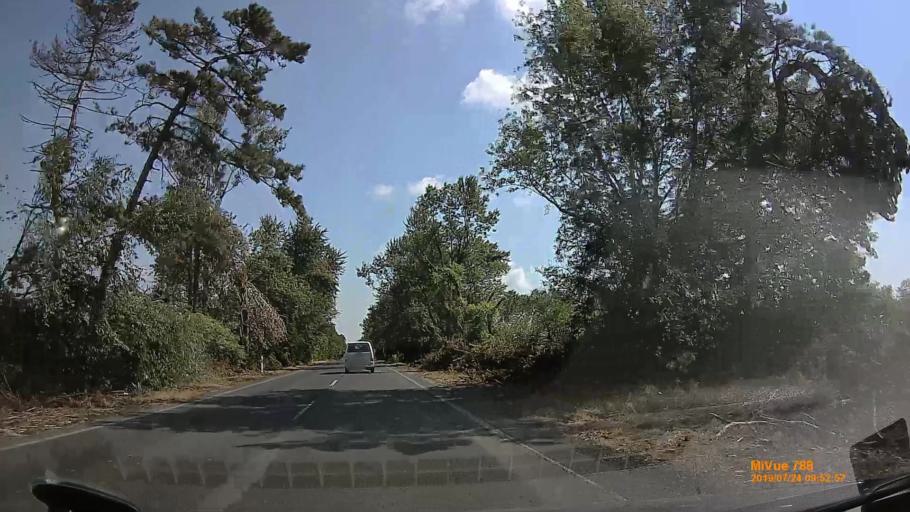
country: HU
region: Szabolcs-Szatmar-Bereg
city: Nyirmada
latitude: 48.0454
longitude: 22.1907
